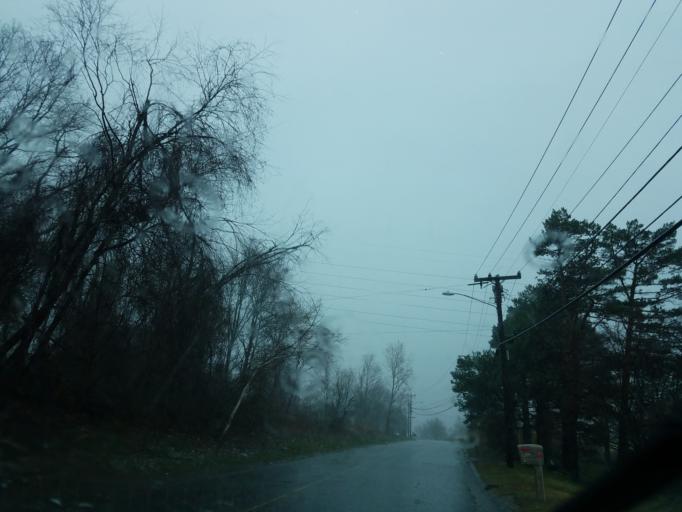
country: US
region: Connecticut
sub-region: New Haven County
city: Waterbury
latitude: 41.5290
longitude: -73.0658
